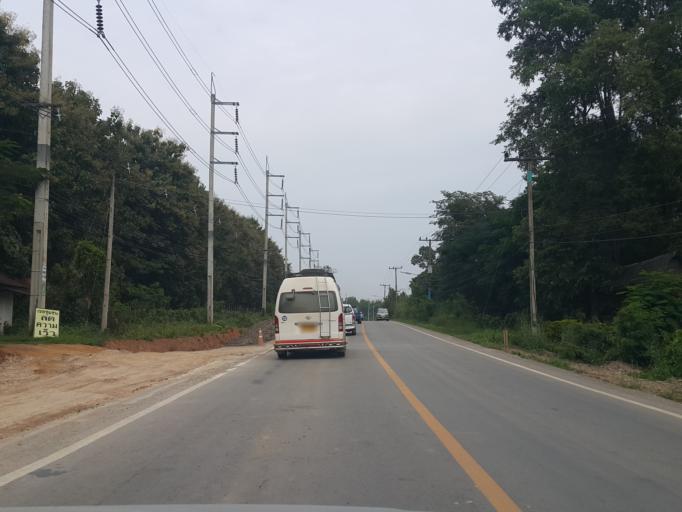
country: TH
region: Chiang Mai
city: Mae Taeng
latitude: 19.0932
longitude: 98.8700
